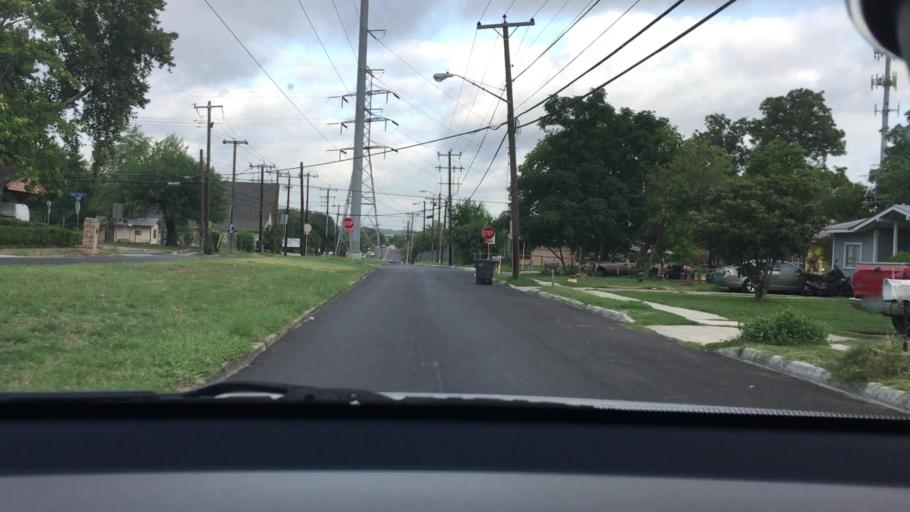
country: US
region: Texas
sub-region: Bexar County
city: Windcrest
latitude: 29.5033
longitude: -98.4059
